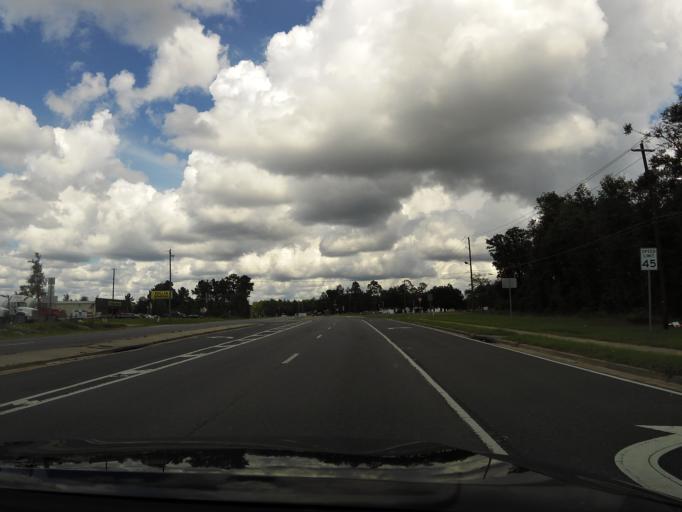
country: US
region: Georgia
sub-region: Charlton County
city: Folkston
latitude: 30.8395
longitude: -82.0065
